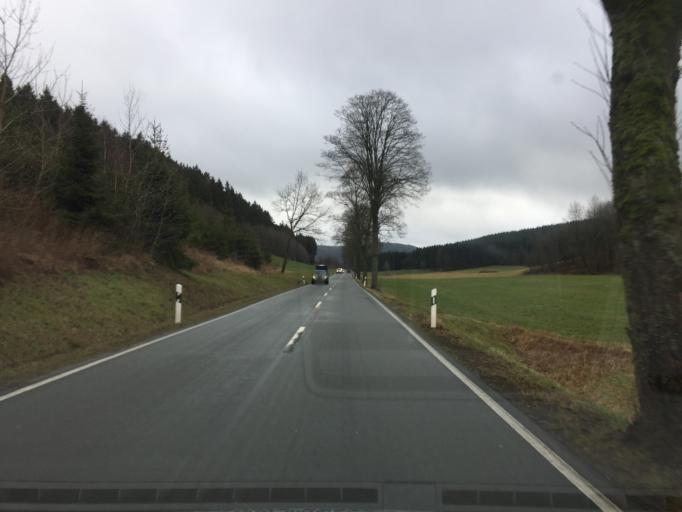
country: DE
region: North Rhine-Westphalia
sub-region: Regierungsbezirk Arnsberg
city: Winterberg
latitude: 51.2256
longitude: 8.5805
